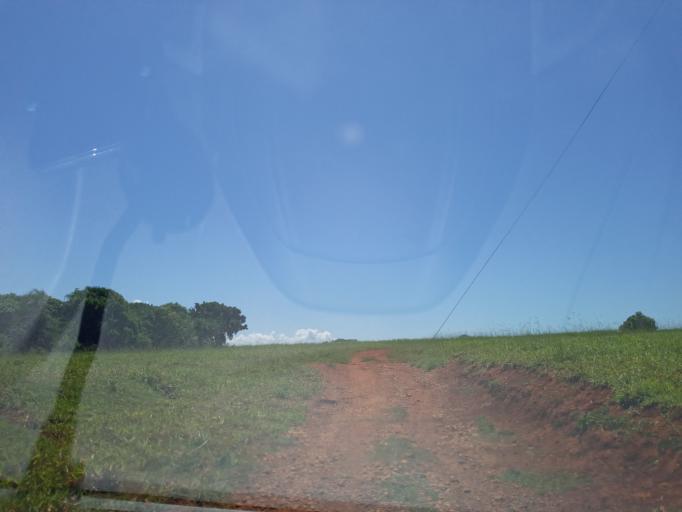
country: BR
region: Goias
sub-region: Itumbiara
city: Itumbiara
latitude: -18.3951
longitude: -49.1255
